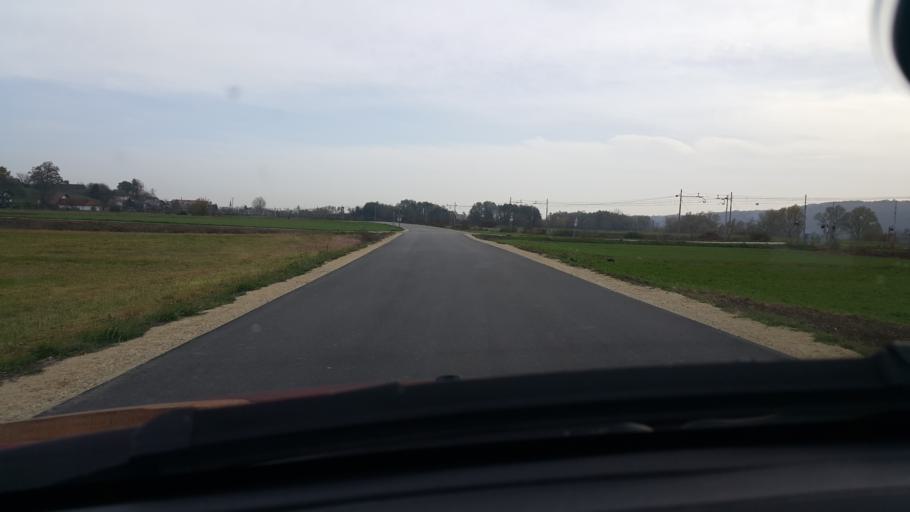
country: SI
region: Brezice
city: Brezice
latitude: 45.9054
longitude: 15.6351
